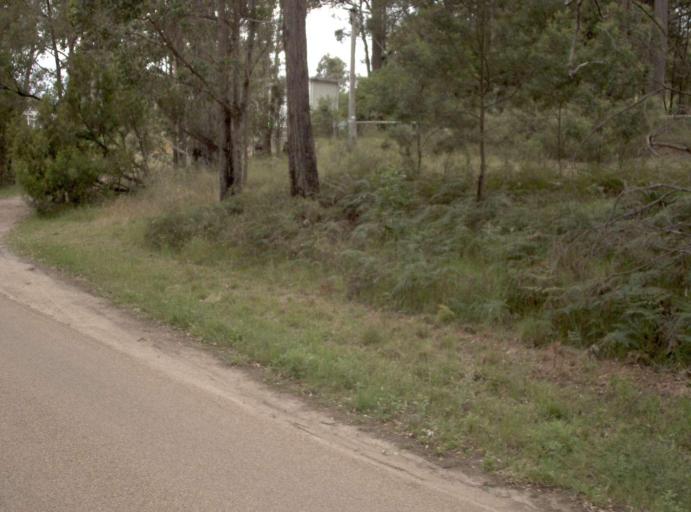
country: AU
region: Victoria
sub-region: East Gippsland
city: Bairnsdale
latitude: -37.7449
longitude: 147.5979
